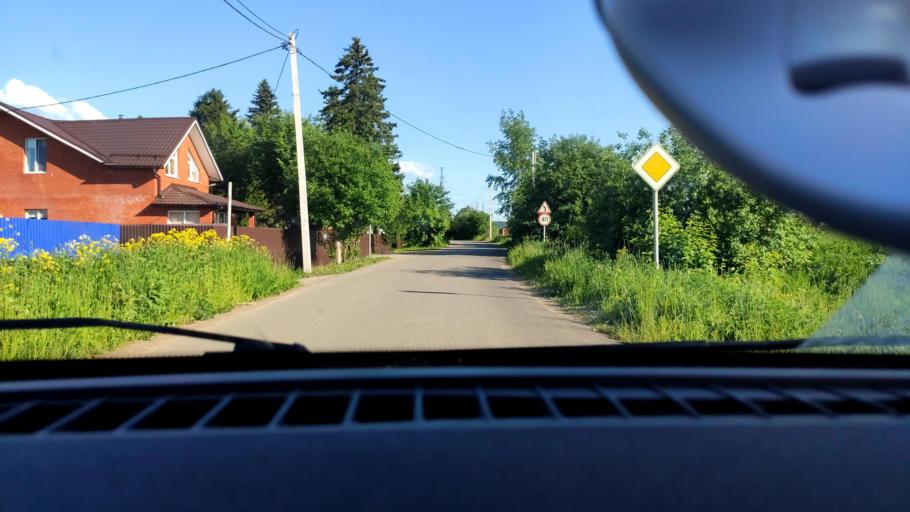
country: RU
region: Perm
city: Ferma
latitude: 57.9182
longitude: 56.3373
